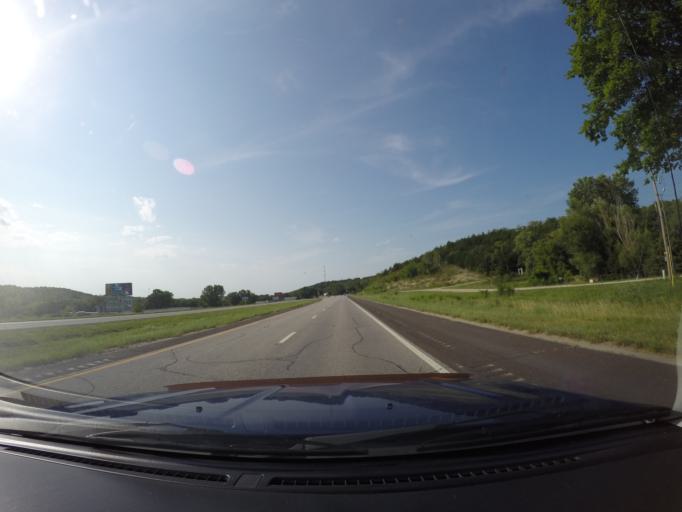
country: US
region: Kansas
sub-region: Riley County
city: Manhattan
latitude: 39.1643
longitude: -96.5398
